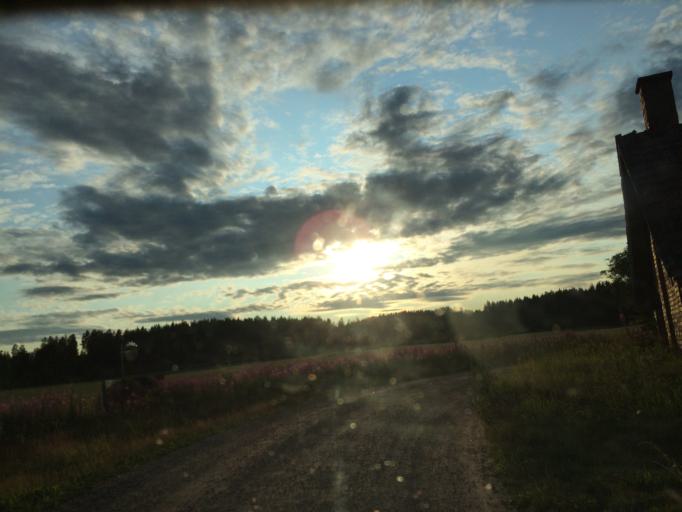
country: FI
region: Haeme
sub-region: Haemeenlinna
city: Janakkala
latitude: 60.8883
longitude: 24.6179
